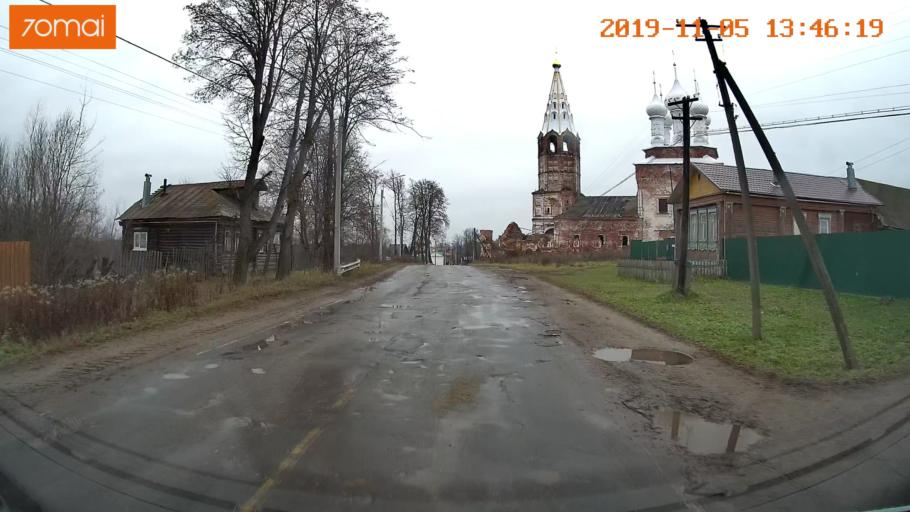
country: RU
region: Ivanovo
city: Shuya
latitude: 56.9948
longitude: 41.4101
